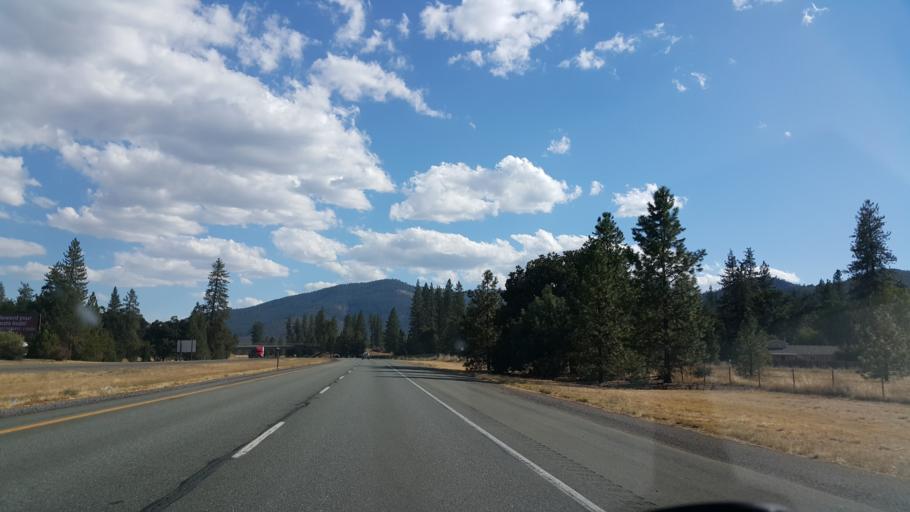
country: US
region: California
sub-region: Siskiyou County
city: Yreka
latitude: 41.6898
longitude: -122.6380
